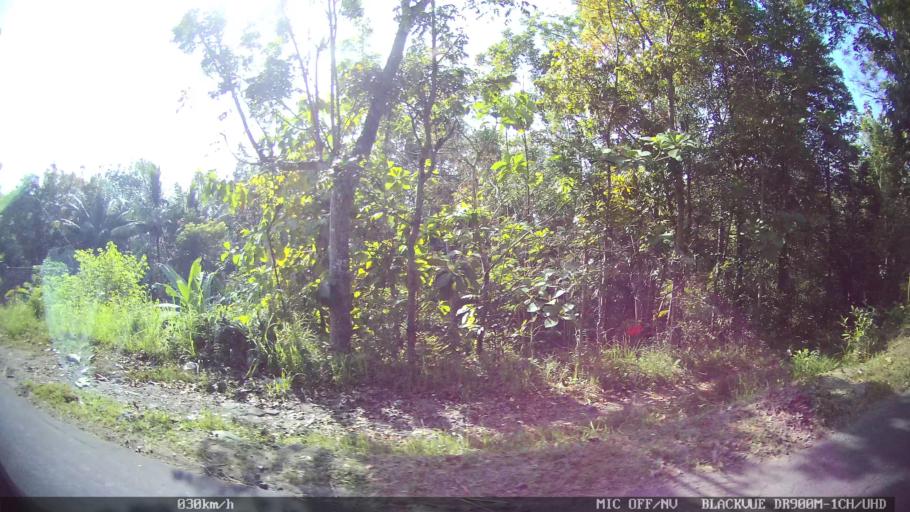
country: ID
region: Daerah Istimewa Yogyakarta
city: Kasihan
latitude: -7.8301
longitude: 110.2881
